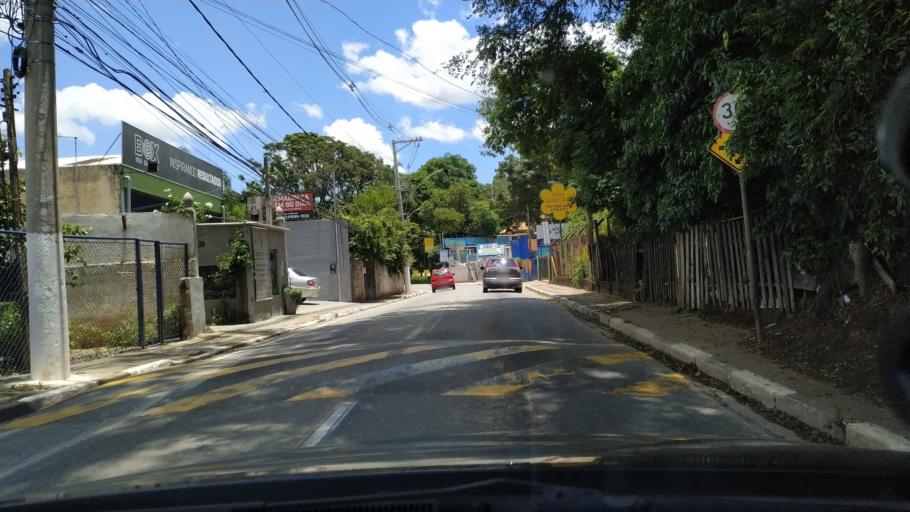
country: BR
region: Sao Paulo
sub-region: Santana De Parnaiba
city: Santana de Parnaiba
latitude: -23.4405
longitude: -46.9118
